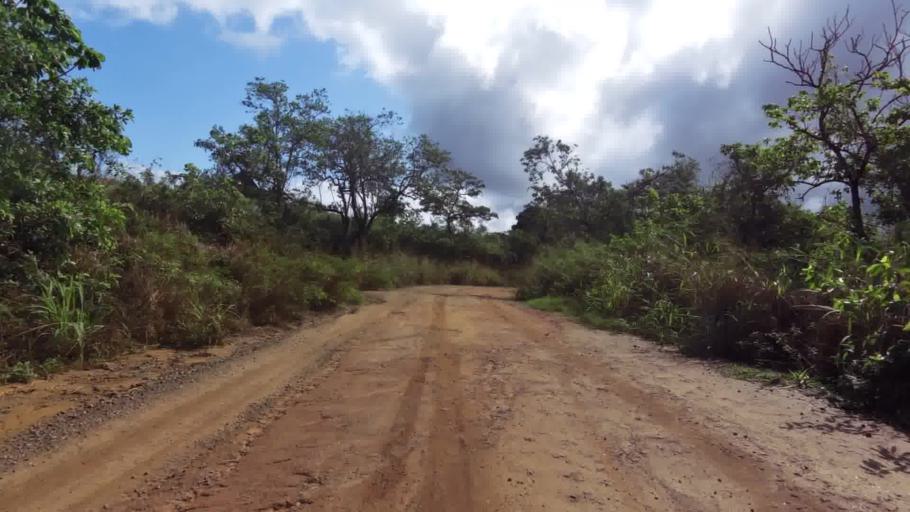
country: BR
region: Espirito Santo
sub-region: Piuma
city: Piuma
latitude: -20.8193
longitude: -40.6789
